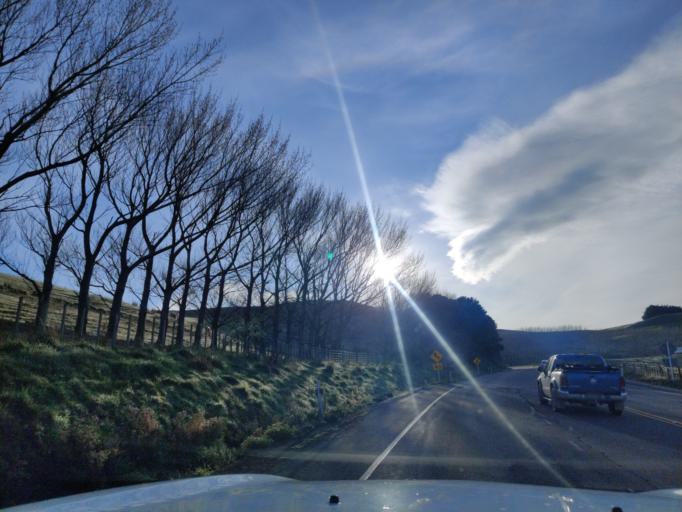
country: NZ
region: Manawatu-Wanganui
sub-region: Palmerston North City
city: Palmerston North
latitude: -40.2856
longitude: 175.7729
